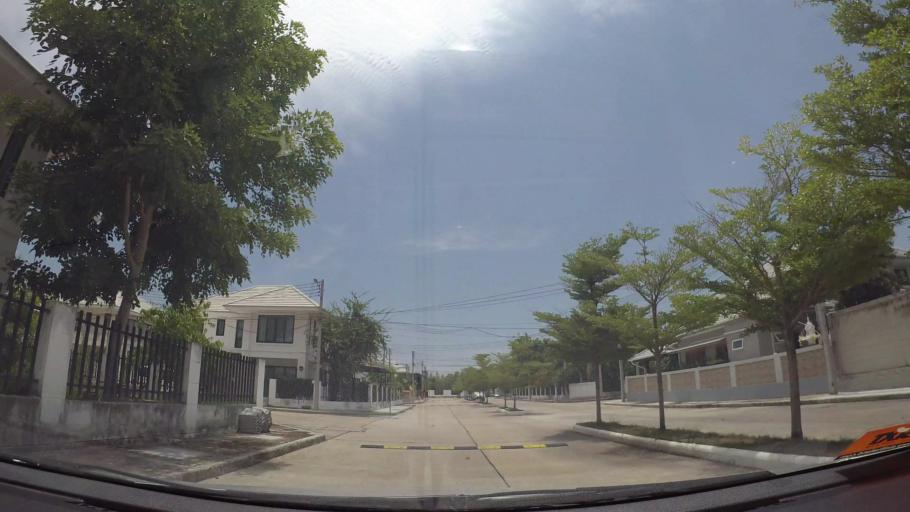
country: TH
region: Chon Buri
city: Chon Buri
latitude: 13.3478
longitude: 100.9623
